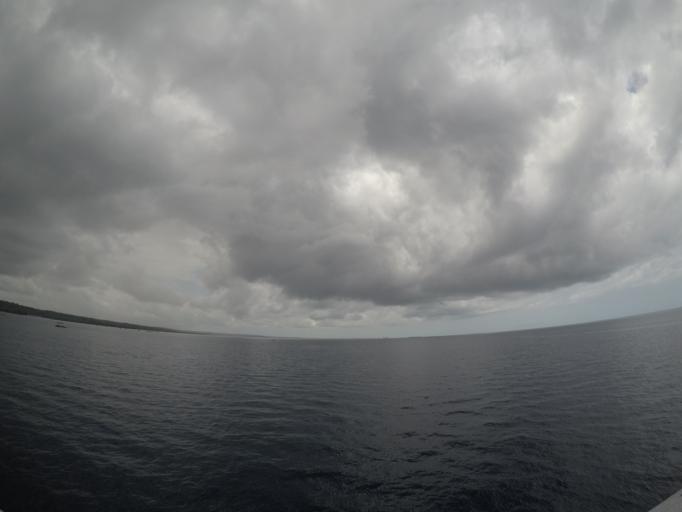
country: TZ
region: Zanzibar North
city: Mkokotoni
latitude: -5.9934
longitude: 39.1750
